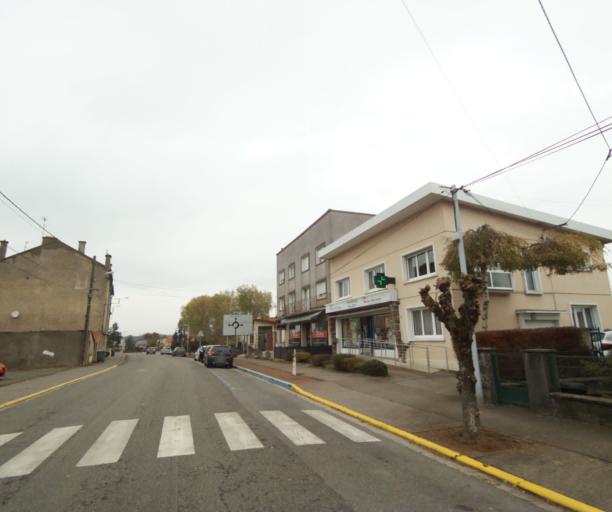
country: FR
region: Lorraine
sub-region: Departement de Meurthe-et-Moselle
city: Mancieulles
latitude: 49.2842
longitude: 5.8949
